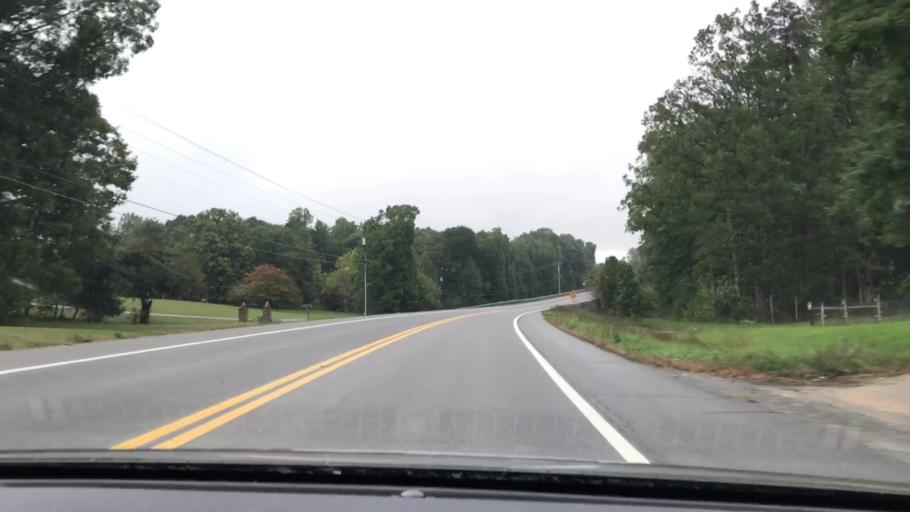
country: US
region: Tennessee
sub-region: Fentress County
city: Grimsley
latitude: 36.2411
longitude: -85.0055
